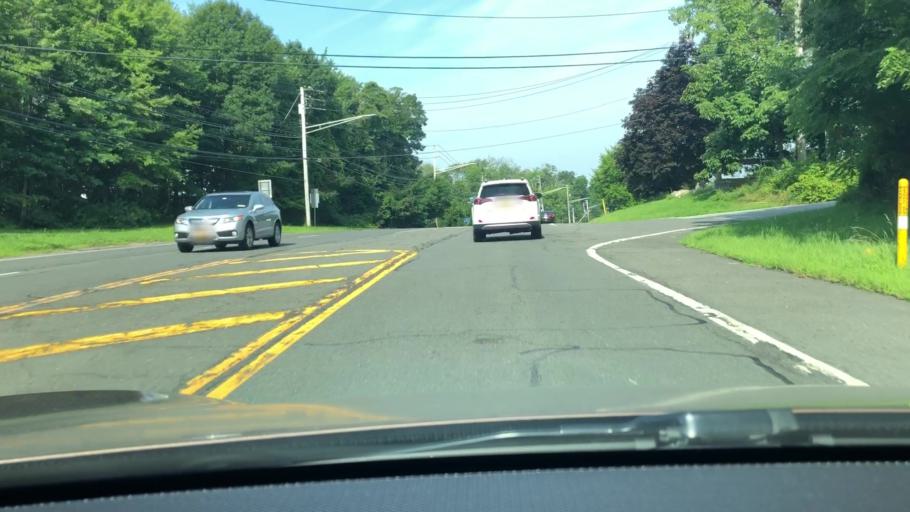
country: US
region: New York
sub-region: Westchester County
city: Elmsford
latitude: 41.0758
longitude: -73.8116
